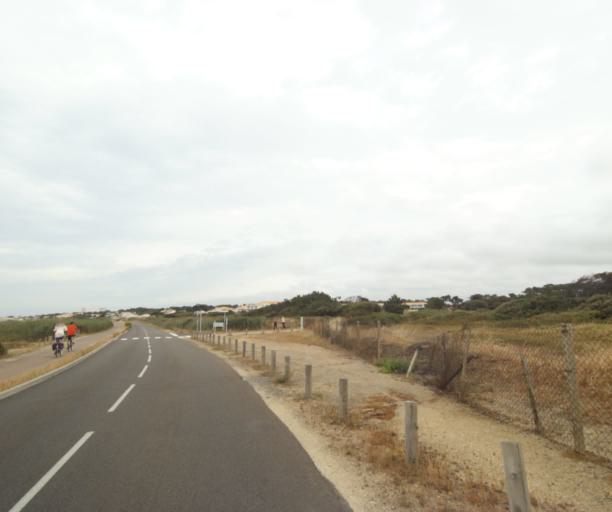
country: FR
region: Pays de la Loire
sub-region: Departement de la Vendee
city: Chateau-d'Olonne
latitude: 46.4700
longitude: -1.7420
